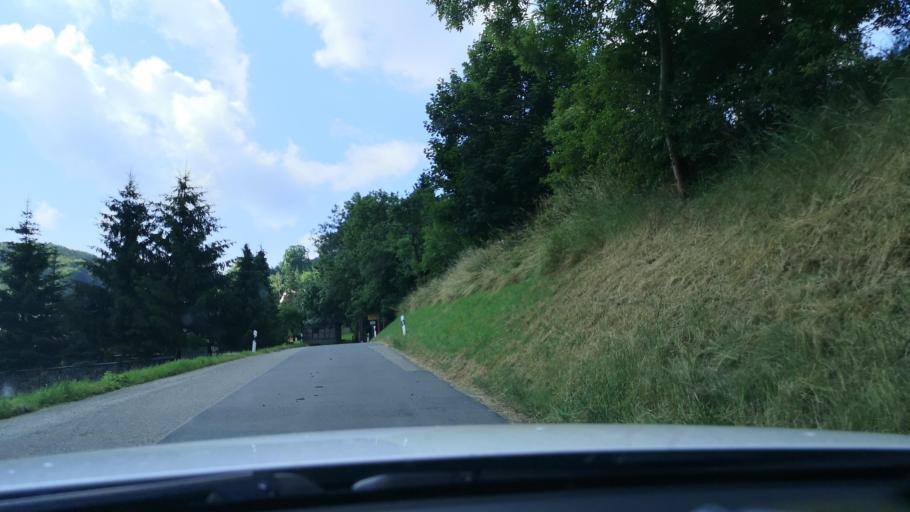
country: DE
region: Thuringia
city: Tautenburg
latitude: 50.9943
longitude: 11.7154
